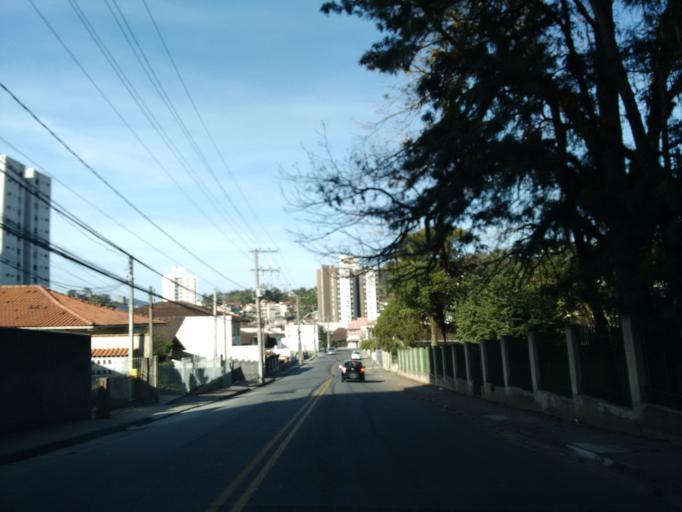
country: BR
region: Santa Catarina
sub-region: Blumenau
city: Blumenau
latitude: -26.8915
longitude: -49.1000
